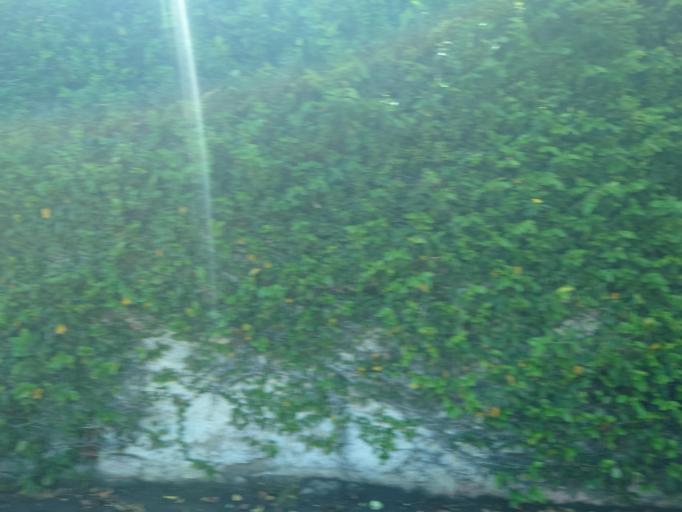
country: NC
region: South Province
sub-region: Noumea
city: Noumea
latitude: -22.2723
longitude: 166.4501
